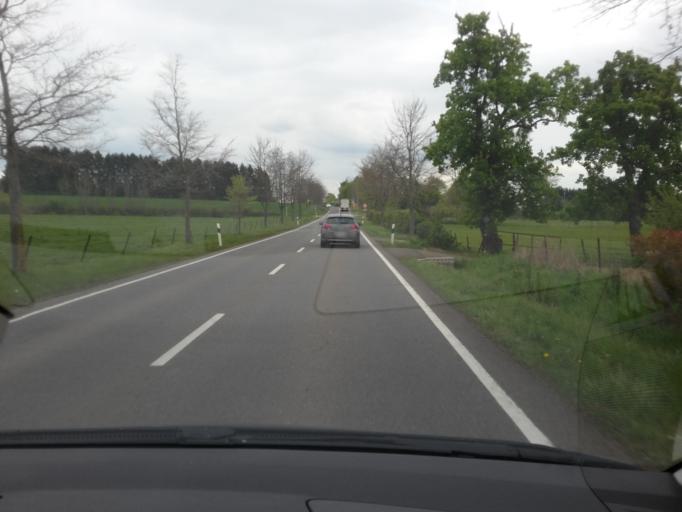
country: LU
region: Luxembourg
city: Schouweiler
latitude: 49.5890
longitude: 5.9671
